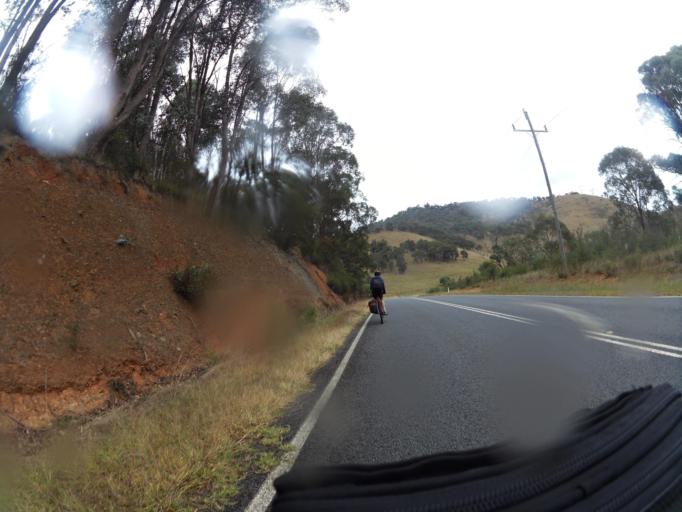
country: AU
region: New South Wales
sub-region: Greater Hume Shire
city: Holbrook
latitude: -36.2203
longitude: 147.6730
